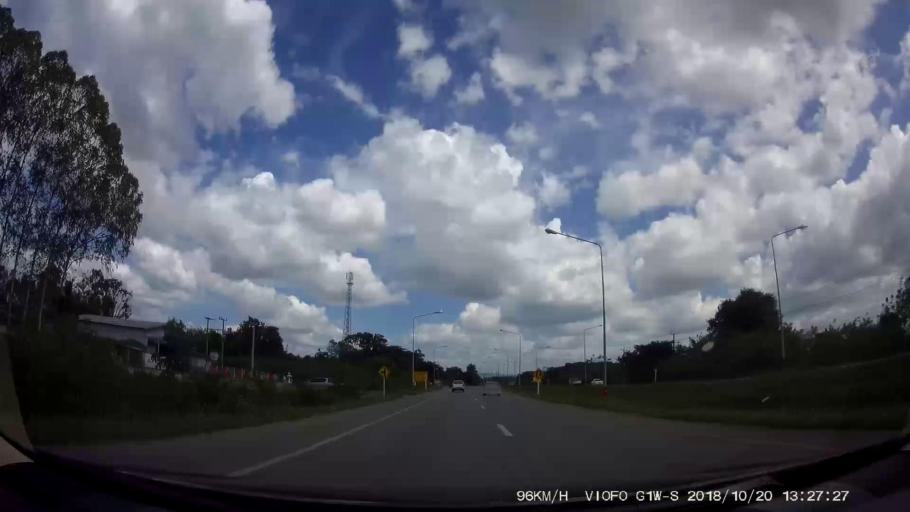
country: TH
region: Chaiyaphum
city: Khon San
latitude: 16.5926
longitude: 101.9606
